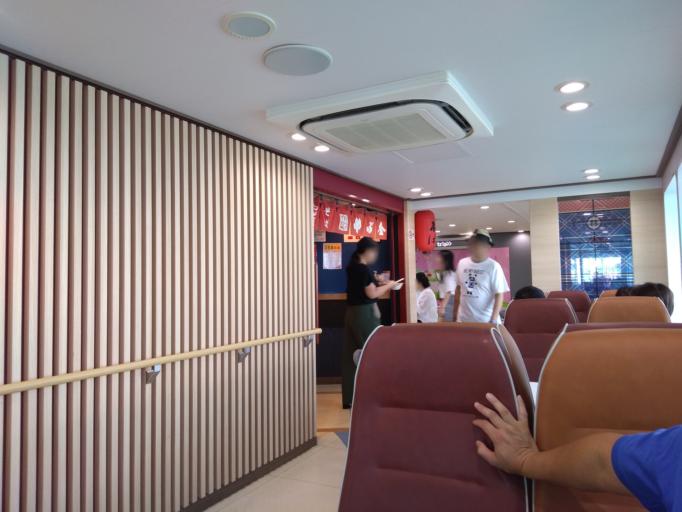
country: JP
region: Kagoshima
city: Kagoshima-shi
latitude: 31.5973
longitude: 130.5635
